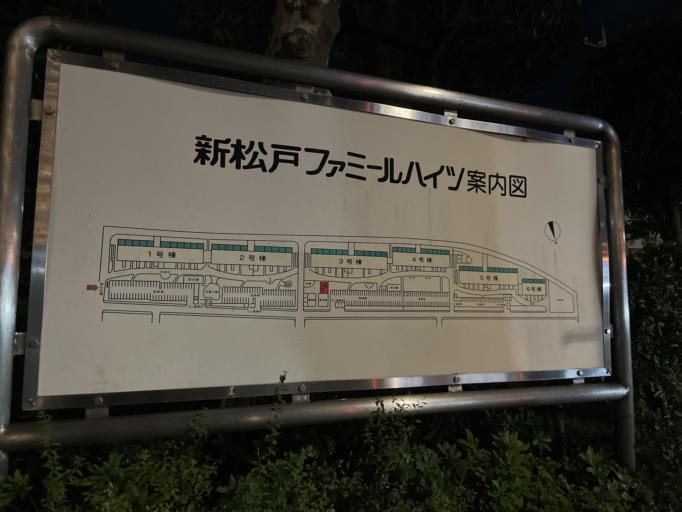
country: JP
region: Chiba
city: Nagareyama
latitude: 35.8304
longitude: 139.9162
